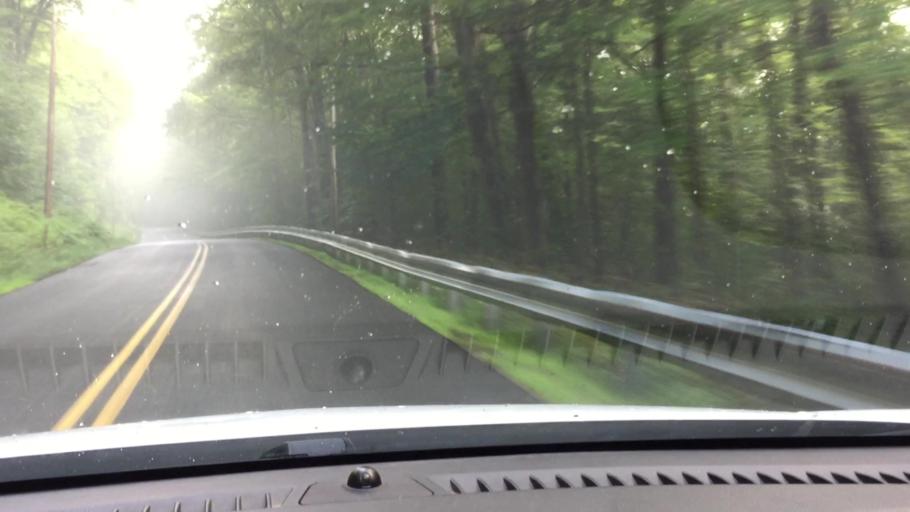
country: US
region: Massachusetts
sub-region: Berkshire County
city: Becket
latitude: 42.4152
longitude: -72.9819
